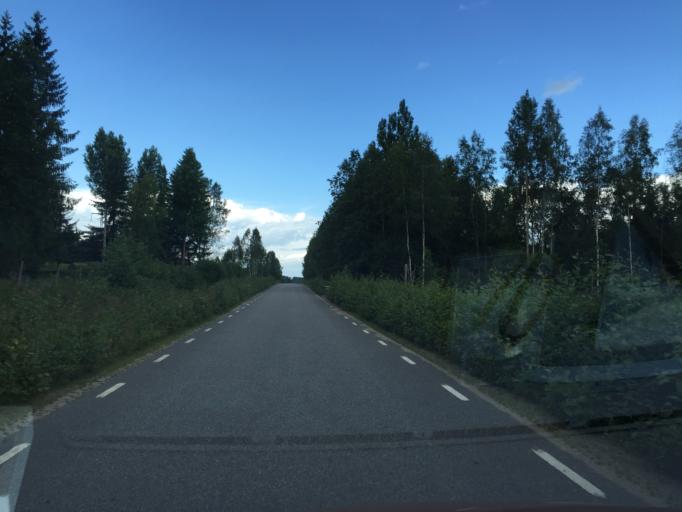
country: SE
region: Gaevleborg
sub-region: Ljusdals Kommun
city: Jaervsoe
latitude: 61.7312
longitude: 16.2841
